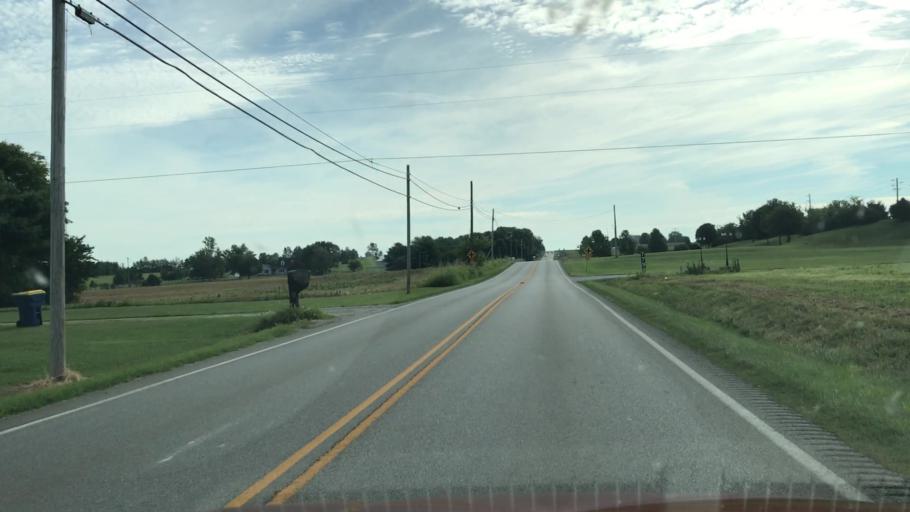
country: US
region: Kentucky
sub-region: Warren County
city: Bowling Green
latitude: 37.0429
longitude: -86.3261
